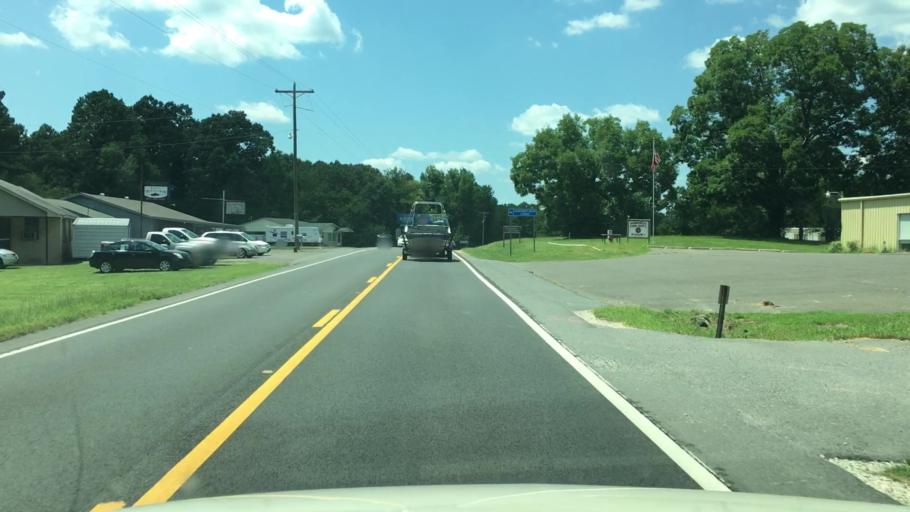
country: US
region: Arkansas
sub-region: Garland County
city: Lake Hamilton
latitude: 34.2680
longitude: -93.1428
